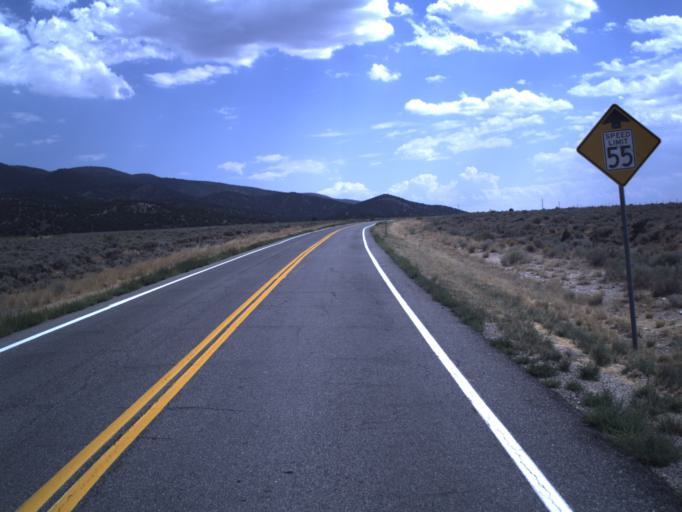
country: US
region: Utah
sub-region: Tooele County
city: Tooele
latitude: 40.3559
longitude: -112.3160
